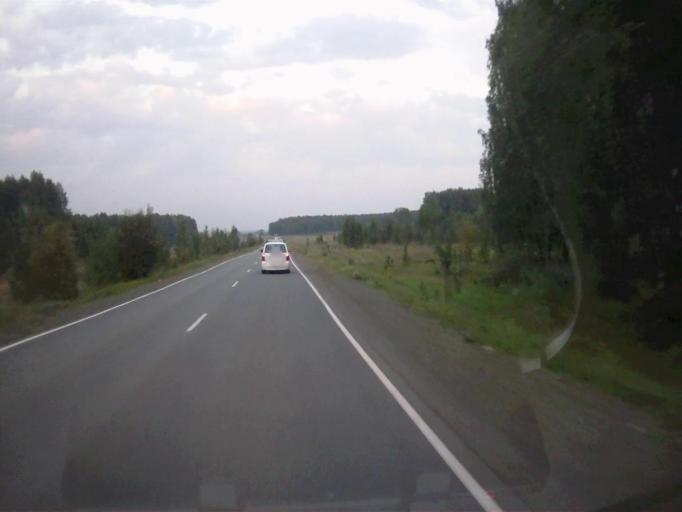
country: RU
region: Chelyabinsk
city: Chebarkul'
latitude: 55.1766
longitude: 60.4587
